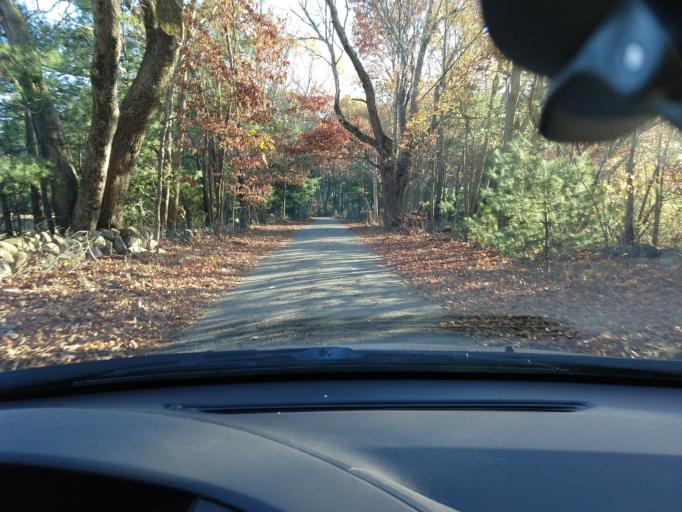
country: US
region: Massachusetts
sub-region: Middlesex County
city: Carlisle
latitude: 42.5067
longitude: -71.3345
